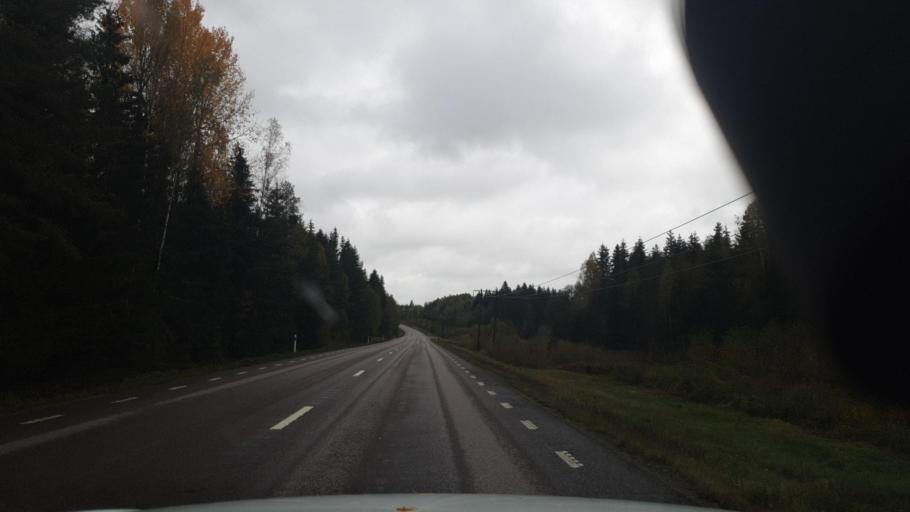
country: SE
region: Vaermland
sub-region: Karlstads Kommun
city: Edsvalla
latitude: 59.4234
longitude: 13.1928
